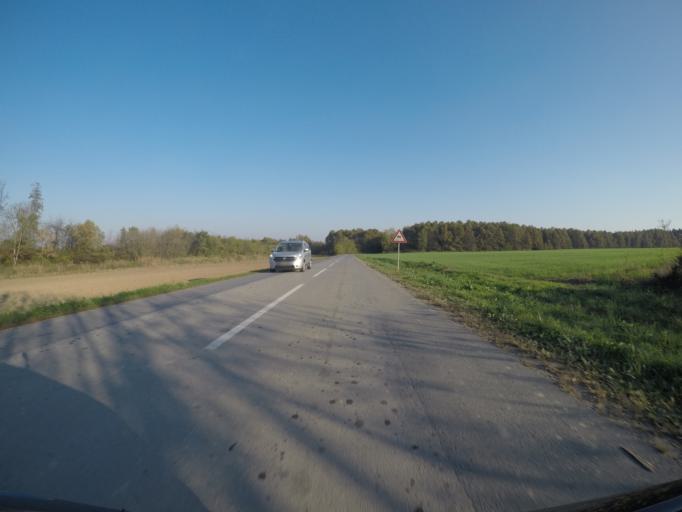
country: HR
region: Virovitick-Podravska
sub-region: Grad Virovitica
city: Virovitica
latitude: 45.8813
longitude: 17.3946
